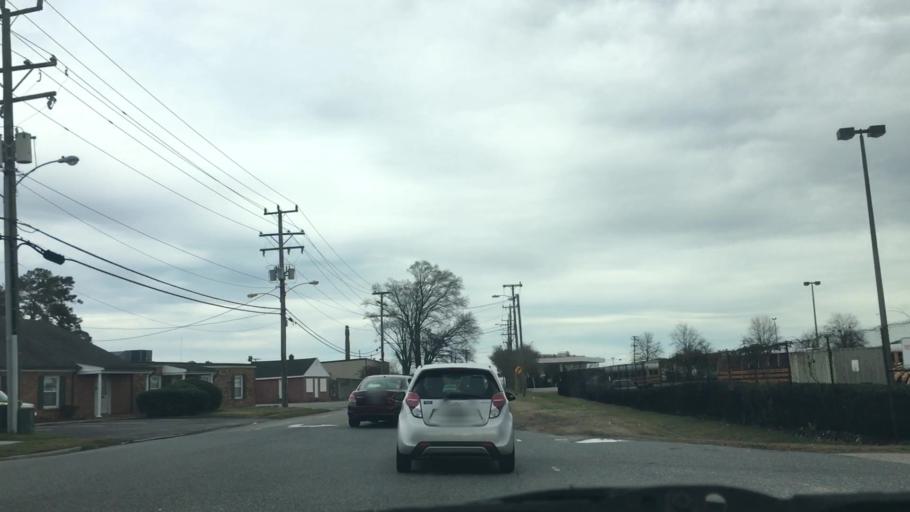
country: US
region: Virginia
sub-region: City of Norfolk
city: Norfolk
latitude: 36.8578
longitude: -76.2182
